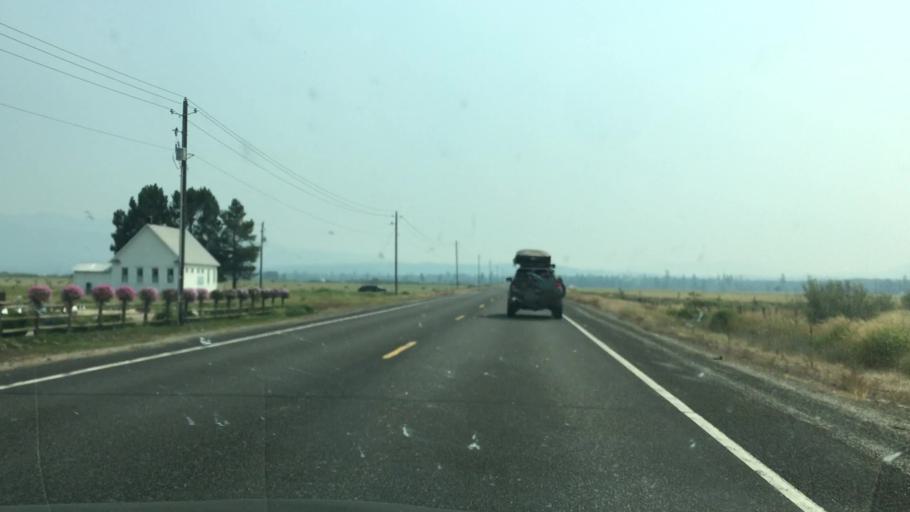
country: US
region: Idaho
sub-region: Valley County
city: Cascade
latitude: 44.4262
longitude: -115.9996
